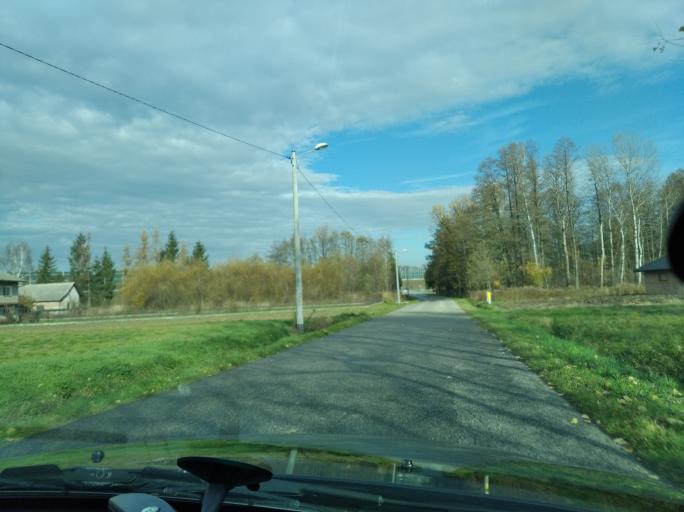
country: PL
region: Subcarpathian Voivodeship
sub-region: Powiat ropczycko-sedziszowski
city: Sedziszow Malopolski
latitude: 50.1073
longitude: 21.6853
